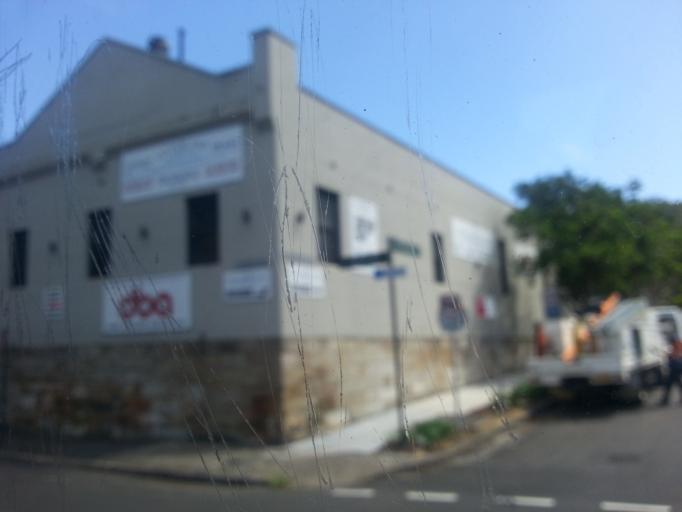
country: AU
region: New South Wales
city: Alexandria
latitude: -33.9104
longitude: 151.2044
